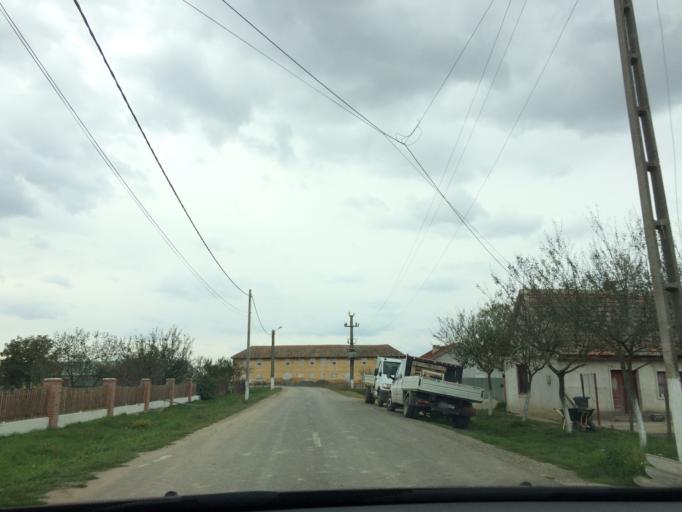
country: RO
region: Timis
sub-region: Oras Recas
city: Recas
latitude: 45.7362
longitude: 21.4886
